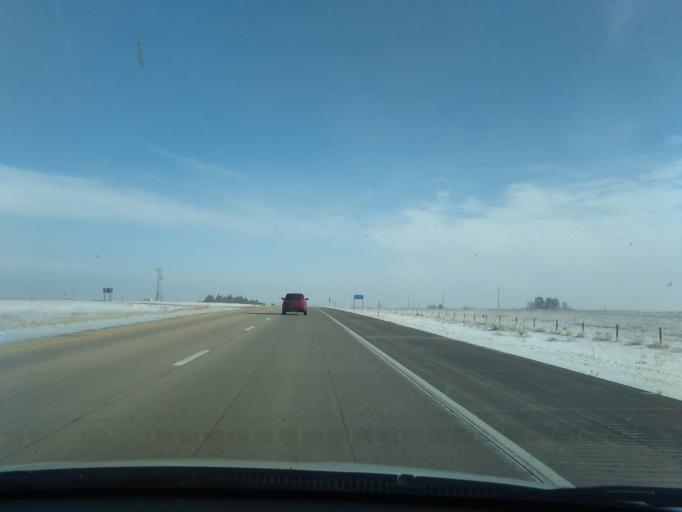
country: US
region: Wyoming
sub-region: Laramie County
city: Pine Bluffs
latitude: 41.1579
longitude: -104.3398
